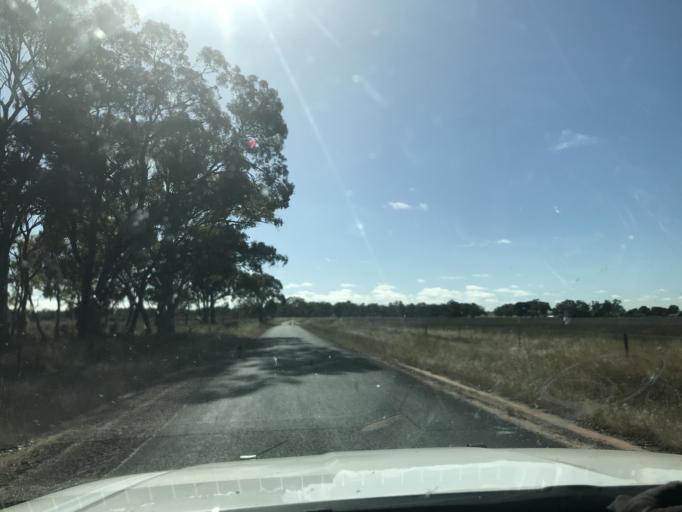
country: AU
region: Victoria
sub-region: Horsham
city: Horsham
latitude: -37.0407
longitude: 141.7380
